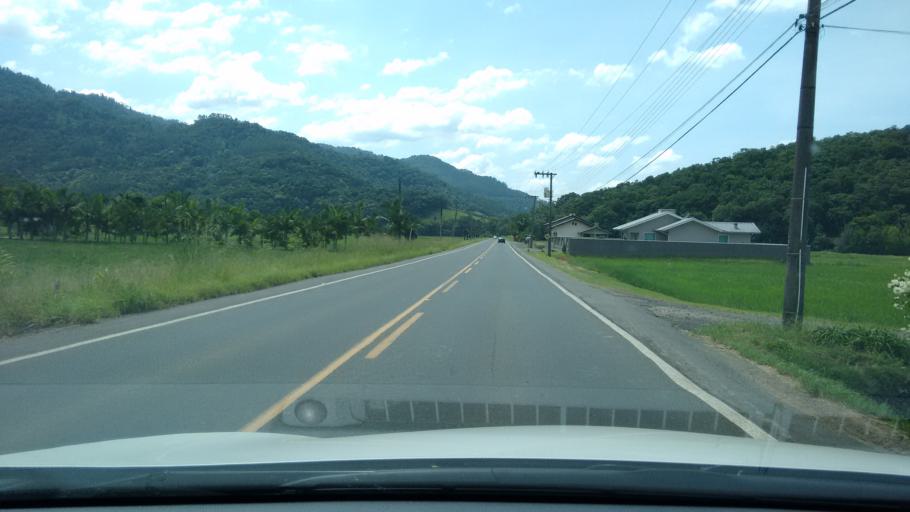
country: BR
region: Santa Catarina
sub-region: Rodeio
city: Gavea
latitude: -26.8853
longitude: -49.3476
